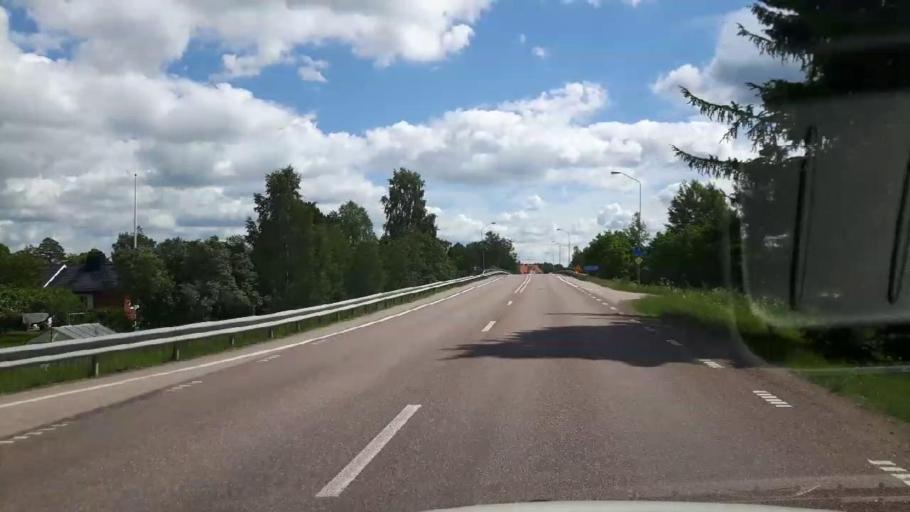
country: SE
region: Dalarna
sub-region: Saters Kommun
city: Saeter
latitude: 60.3977
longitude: 15.8822
